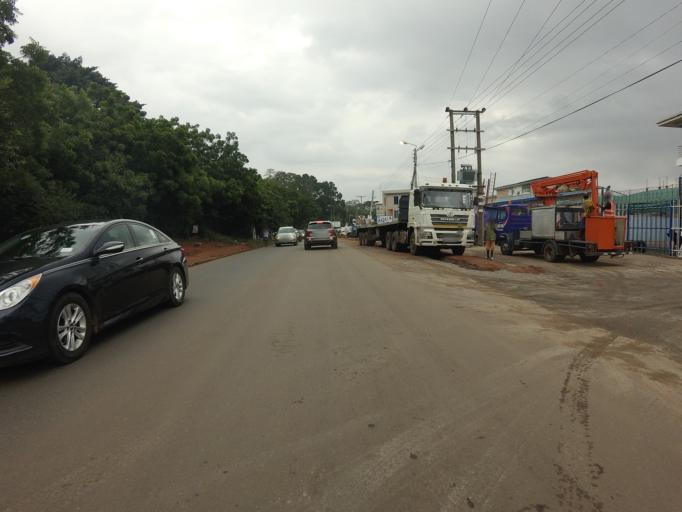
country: GH
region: Greater Accra
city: Dome
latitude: 5.6305
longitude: -0.2192
